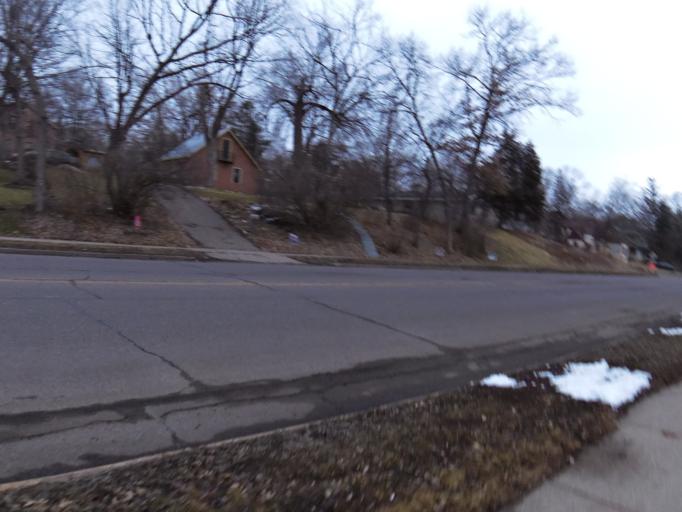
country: US
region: Wisconsin
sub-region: Saint Croix County
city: Hudson
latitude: 44.9811
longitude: -92.7573
